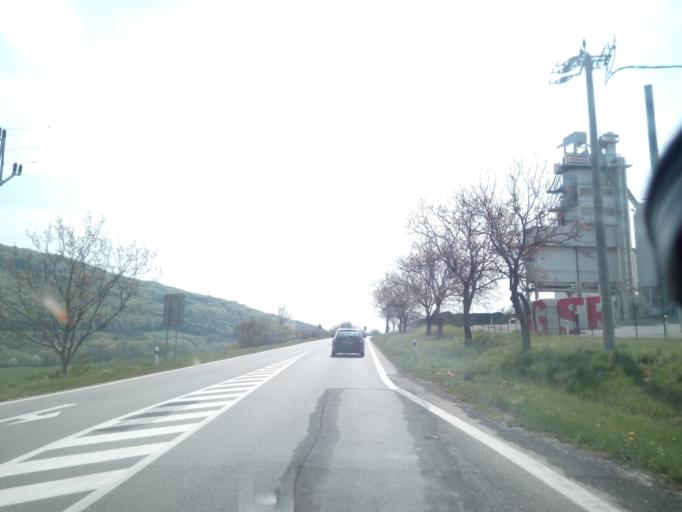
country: SK
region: Presovsky
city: Giraltovce
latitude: 49.0290
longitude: 21.5249
